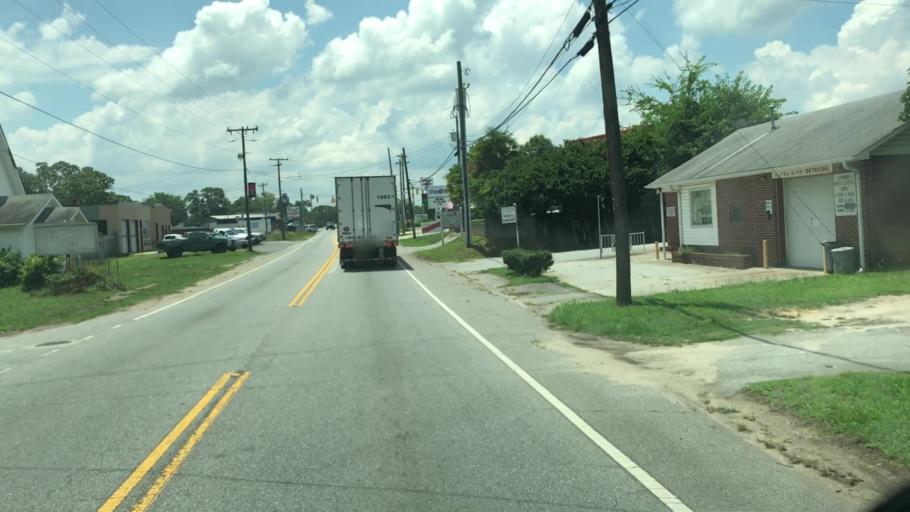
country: US
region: South Carolina
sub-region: Anderson County
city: Williamston
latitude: 34.6239
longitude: -82.4709
